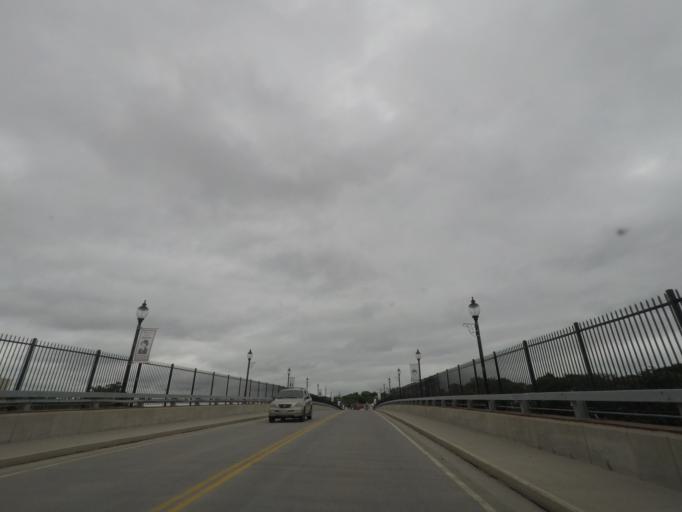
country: US
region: New York
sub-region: Rensselaer County
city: Rensselaer
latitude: 42.6450
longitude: -73.7410
